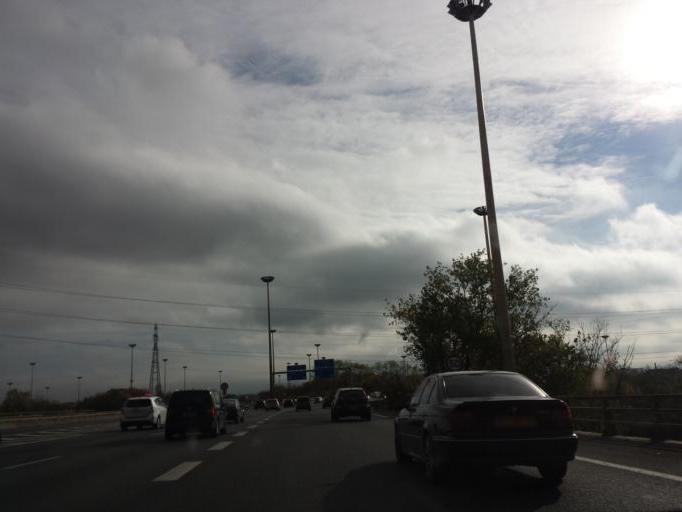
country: FR
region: Ile-de-France
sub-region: Departement des Hauts-de-Seine
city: Gennevilliers
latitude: 48.9406
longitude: 2.2924
